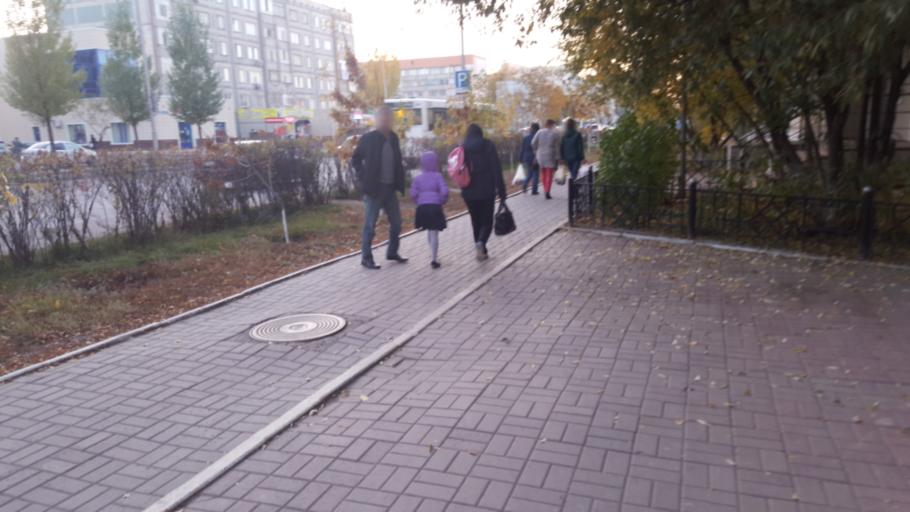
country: KZ
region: Astana Qalasy
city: Astana
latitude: 51.1539
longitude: 71.5056
